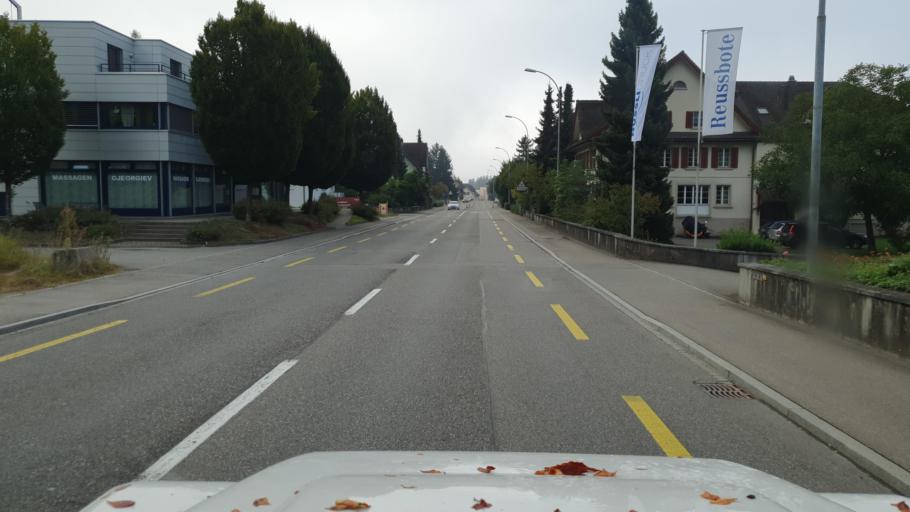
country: CH
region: Aargau
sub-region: Bezirk Baden
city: Mellingen
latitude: 47.4232
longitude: 8.2724
